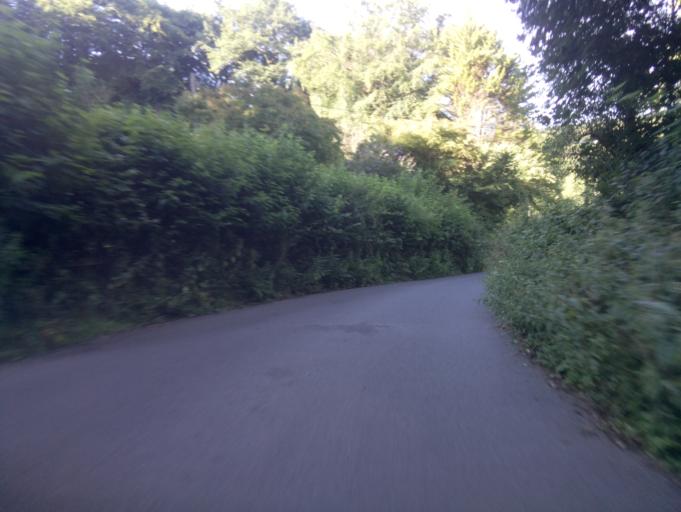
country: GB
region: Wales
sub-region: Monmouthshire
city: Tintern
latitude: 51.7165
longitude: -2.6885
